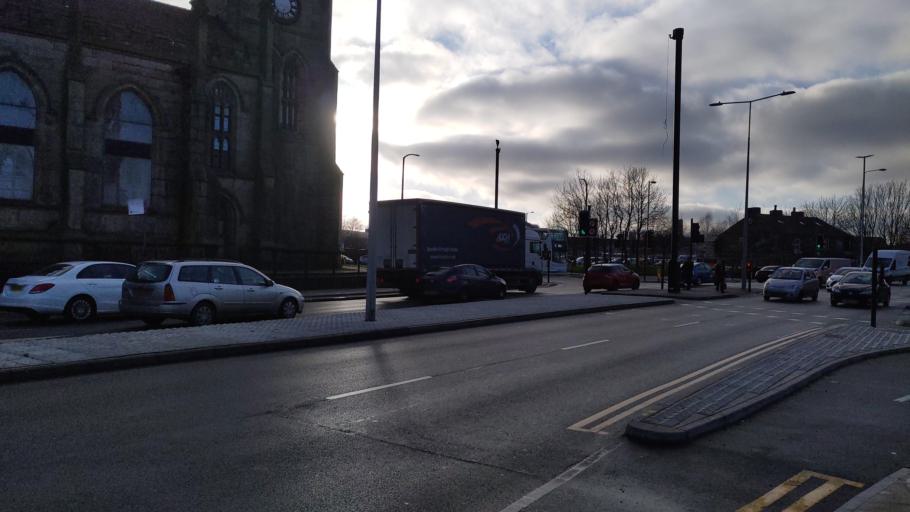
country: GB
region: England
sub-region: Borough of Bolton
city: Bolton
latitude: 53.5743
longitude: -2.4268
